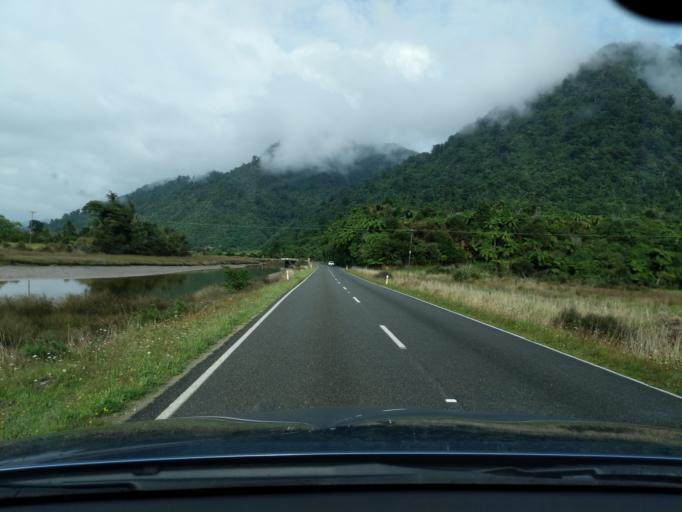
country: NZ
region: Tasman
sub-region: Tasman District
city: Takaka
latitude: -40.6545
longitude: 172.6500
